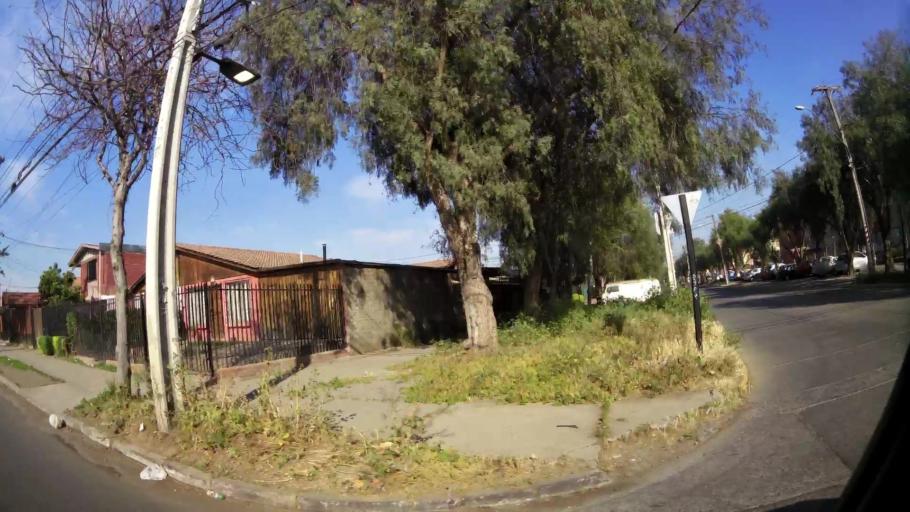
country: CL
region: Santiago Metropolitan
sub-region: Provincia de Santiago
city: Lo Prado
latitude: -33.4587
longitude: -70.7314
